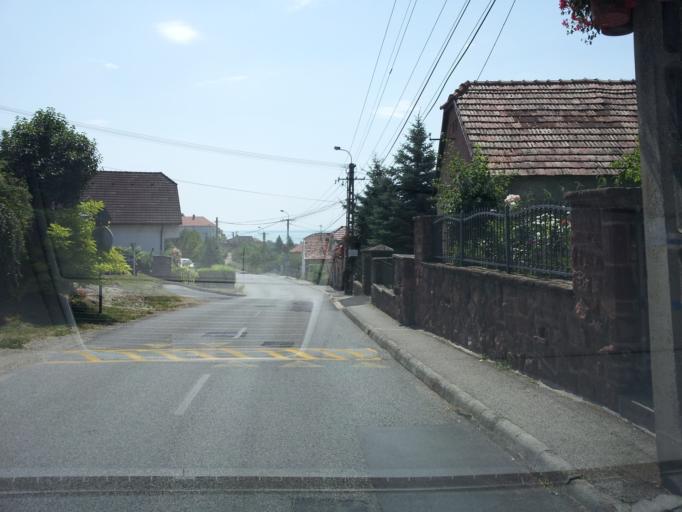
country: HU
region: Veszprem
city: Csopak
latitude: 46.9944
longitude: 17.9696
